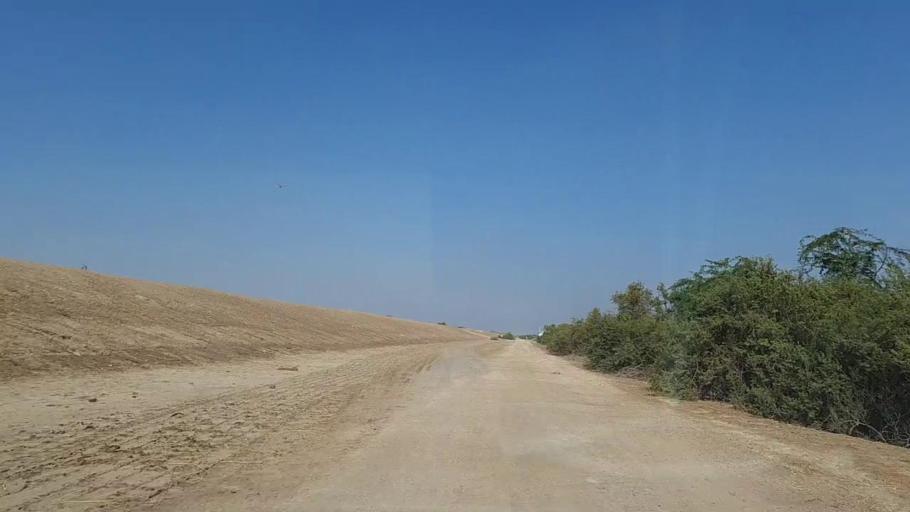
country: PK
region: Sindh
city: Chuhar Jamali
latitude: 24.4630
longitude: 68.0036
